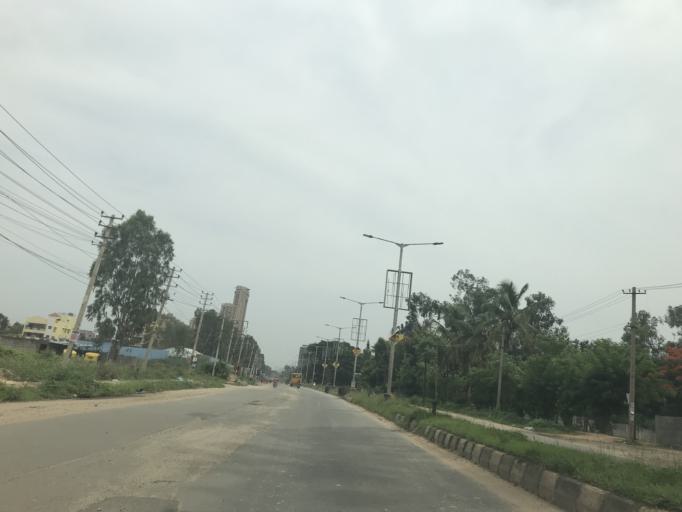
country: IN
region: Karnataka
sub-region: Bangalore Urban
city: Yelahanka
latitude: 13.0733
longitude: 77.6515
